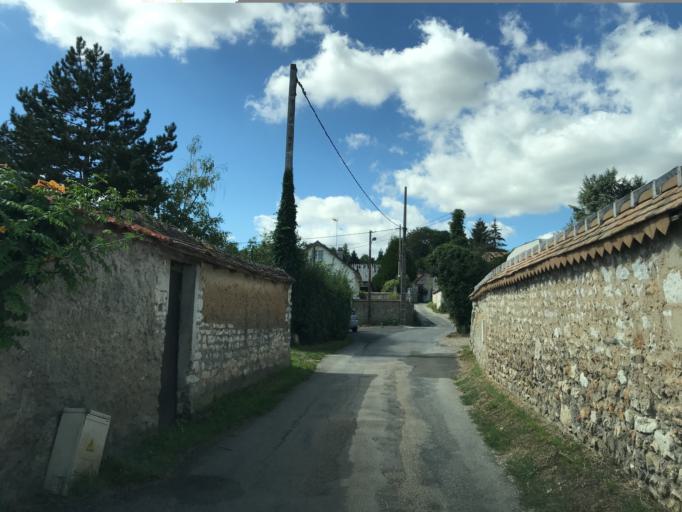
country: FR
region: Haute-Normandie
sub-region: Departement de l'Eure
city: Saint-Just
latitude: 49.1426
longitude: 1.4129
